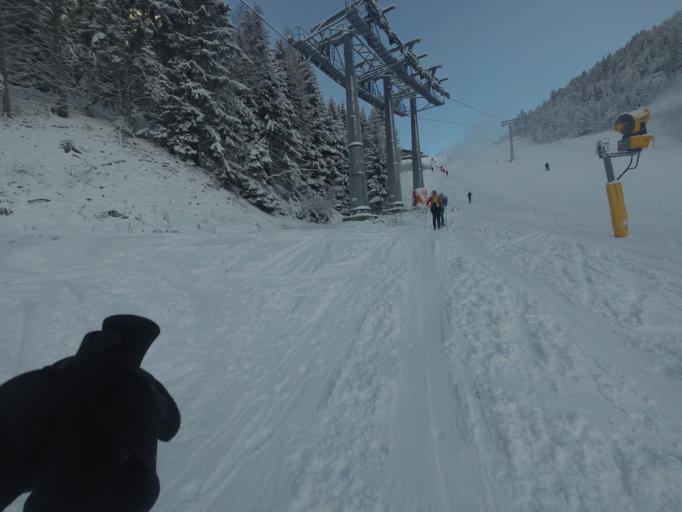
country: AT
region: Salzburg
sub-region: Politischer Bezirk Sankt Johann im Pongau
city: Sankt Johann im Pongau
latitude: 47.3176
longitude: 13.2157
